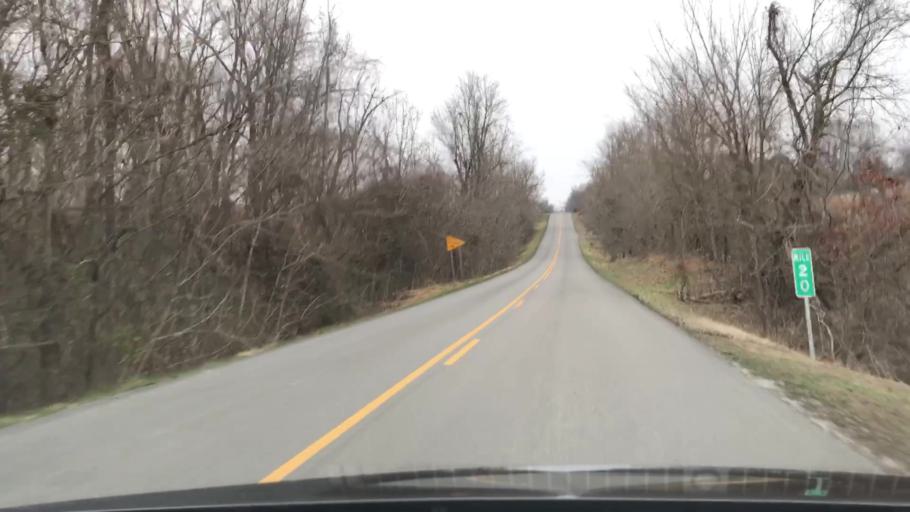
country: US
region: Kentucky
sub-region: Muhlenberg County
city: Morehead
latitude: 37.3169
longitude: -87.2184
